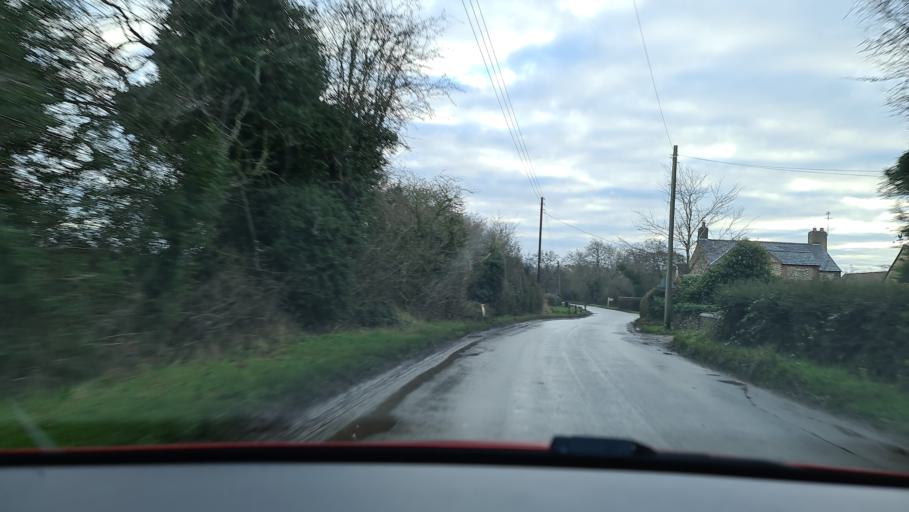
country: GB
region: England
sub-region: Buckinghamshire
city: Great Missenden
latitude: 51.7334
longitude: -0.6697
